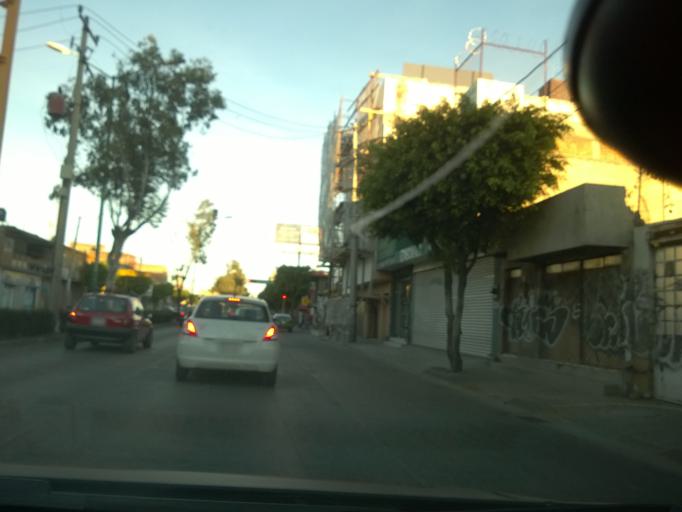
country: MX
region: Guanajuato
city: Leon
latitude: 21.1151
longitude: -101.6843
